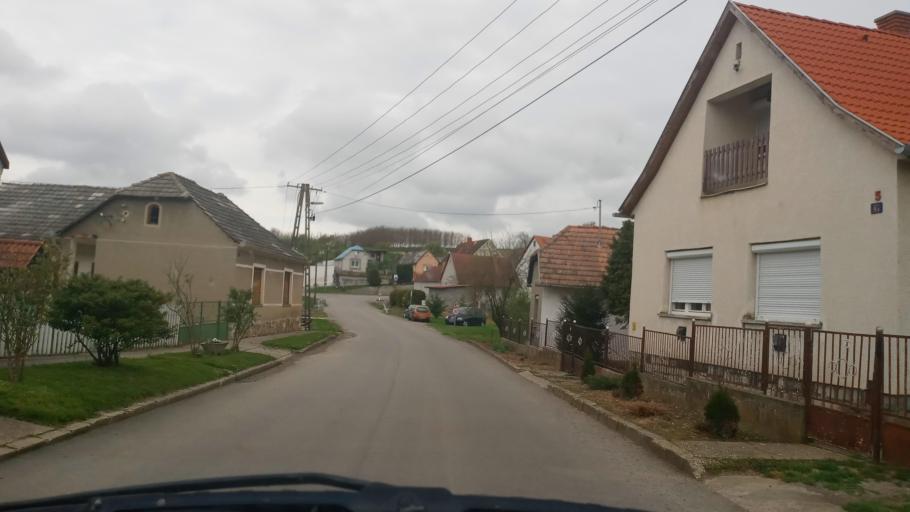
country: HU
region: Baranya
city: Kozarmisleny
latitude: 46.0406
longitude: 18.3490
